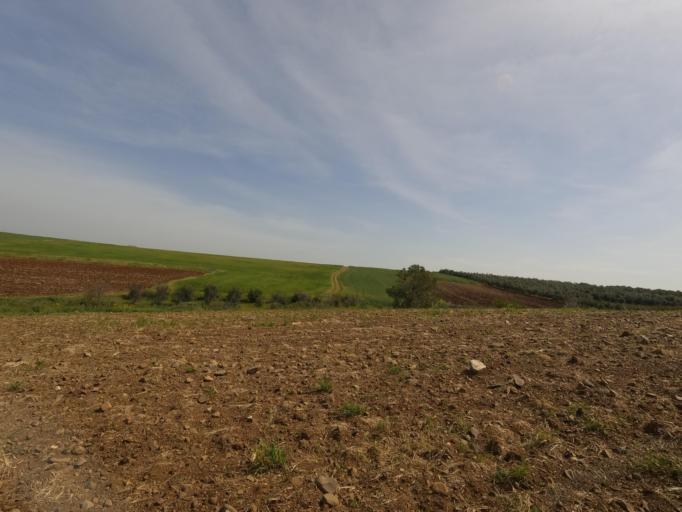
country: CY
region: Lefkosia
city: Astromeritis
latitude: 35.1037
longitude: 32.9623
